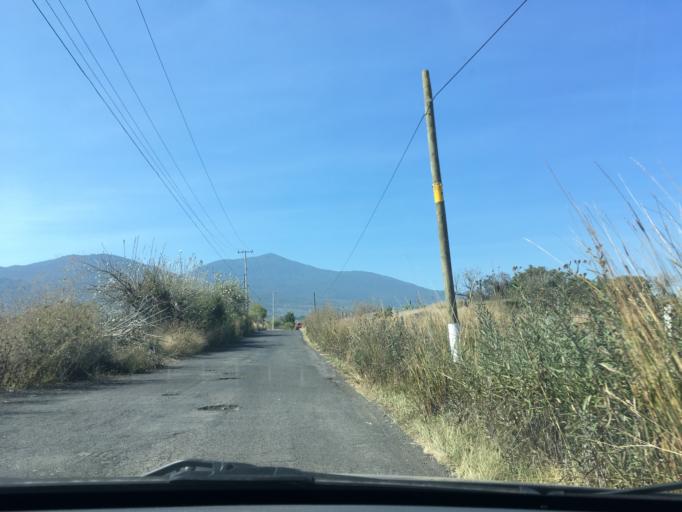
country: MX
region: Michoacan
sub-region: Morelia
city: La Mintzita (Piedra Dura)
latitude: 19.6486
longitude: -101.3005
